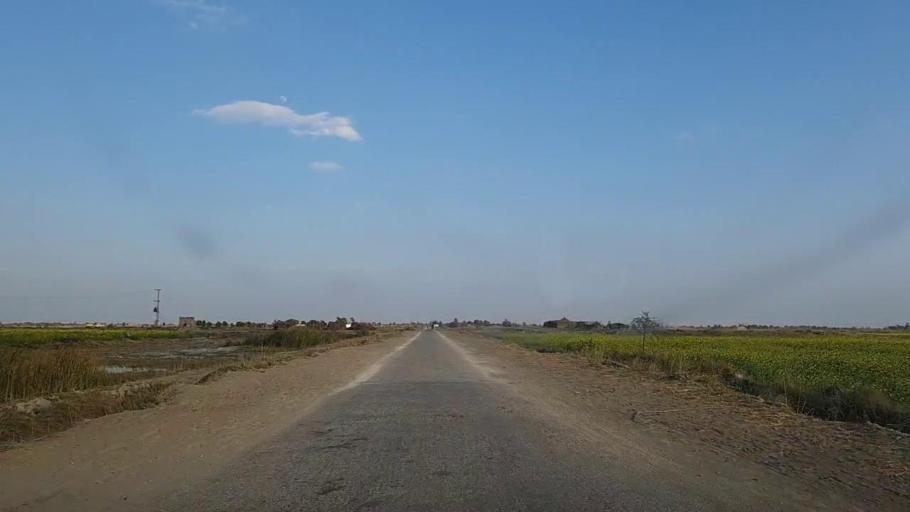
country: PK
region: Sindh
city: Sanghar
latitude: 26.2644
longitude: 68.9468
